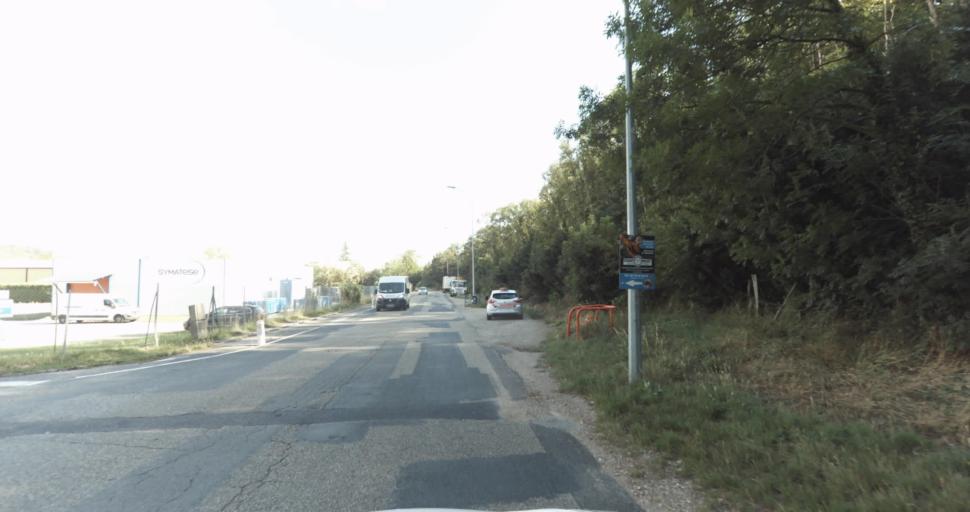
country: FR
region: Rhone-Alpes
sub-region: Departement du Rhone
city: Chaponost
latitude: 45.6966
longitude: 4.7613
